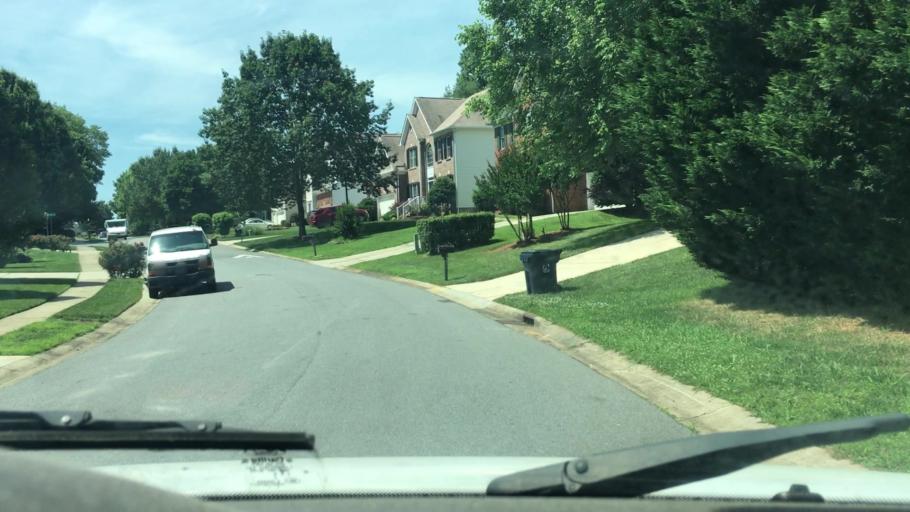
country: US
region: North Carolina
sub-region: Mecklenburg County
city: Huntersville
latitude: 35.4438
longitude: -80.8526
